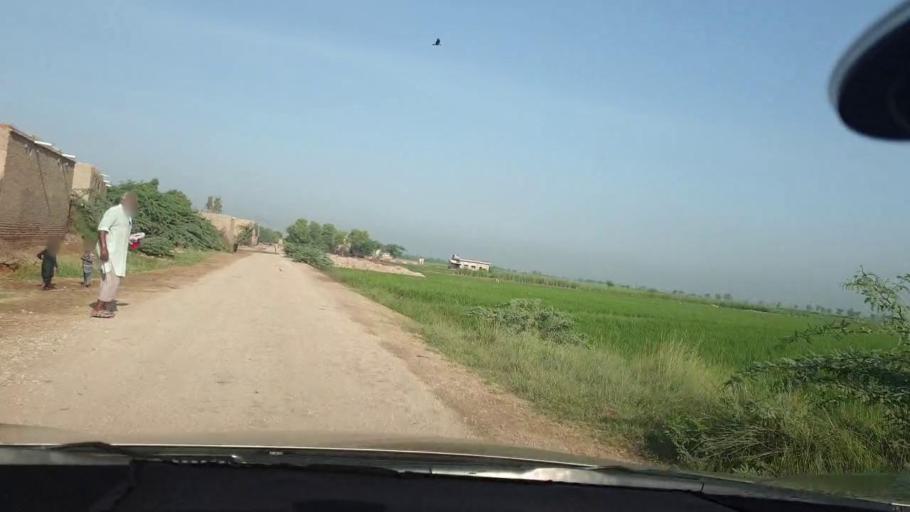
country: PK
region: Sindh
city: Kambar
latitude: 27.6544
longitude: 68.0327
